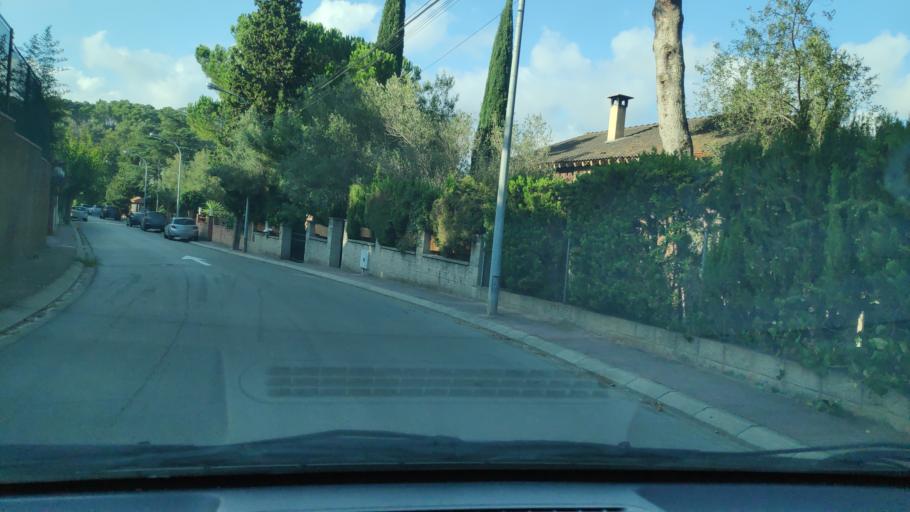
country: ES
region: Catalonia
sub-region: Provincia de Barcelona
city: Sant Quirze del Valles
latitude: 41.5064
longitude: 2.0927
